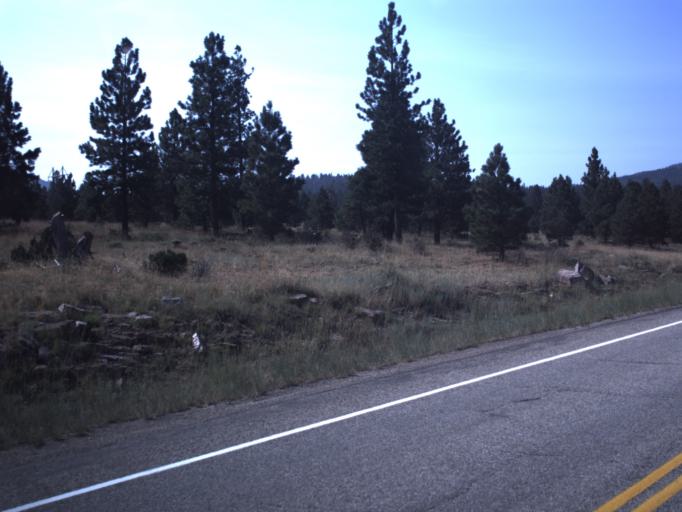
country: US
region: Utah
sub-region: Daggett County
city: Manila
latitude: 40.8785
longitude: -109.4627
